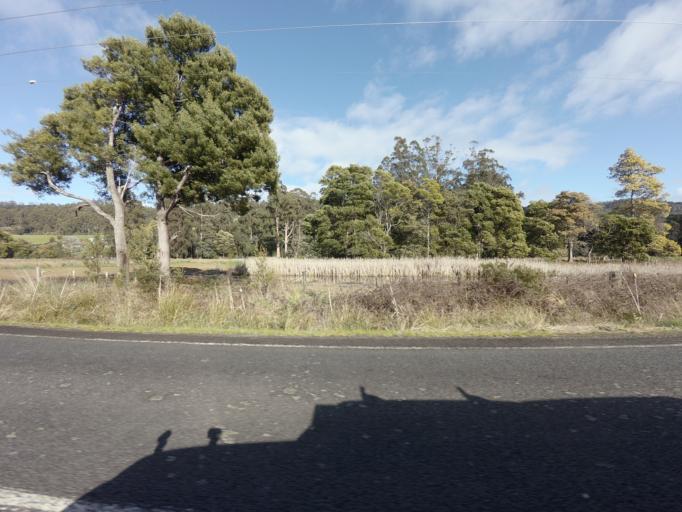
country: AU
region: Tasmania
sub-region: Huon Valley
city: Cygnet
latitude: -43.2905
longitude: 147.0108
